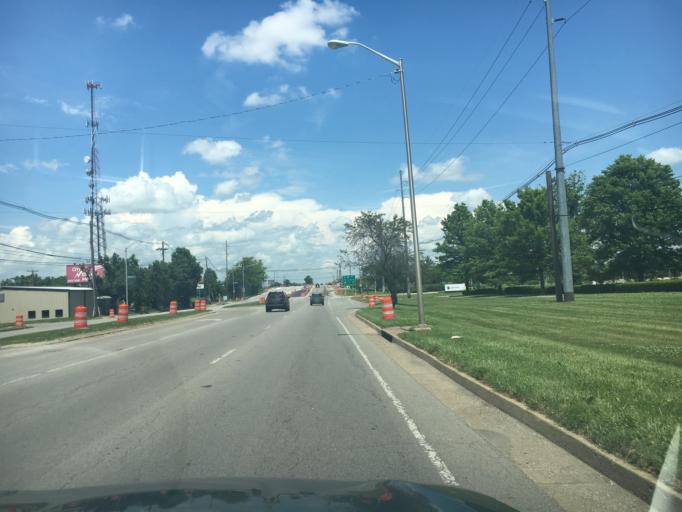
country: US
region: Kentucky
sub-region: Fayette County
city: Lexington-Fayette
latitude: 38.0705
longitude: -84.4968
